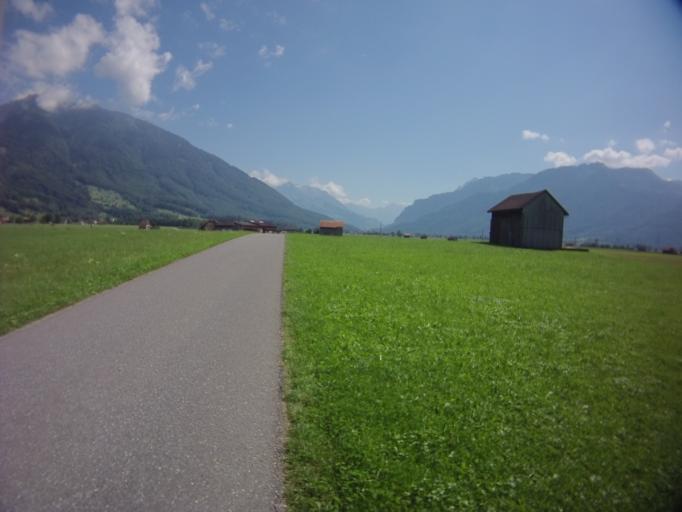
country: CH
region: Saint Gallen
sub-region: Wahlkreis See-Gaster
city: Schanis
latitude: 47.1861
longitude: 9.0376
